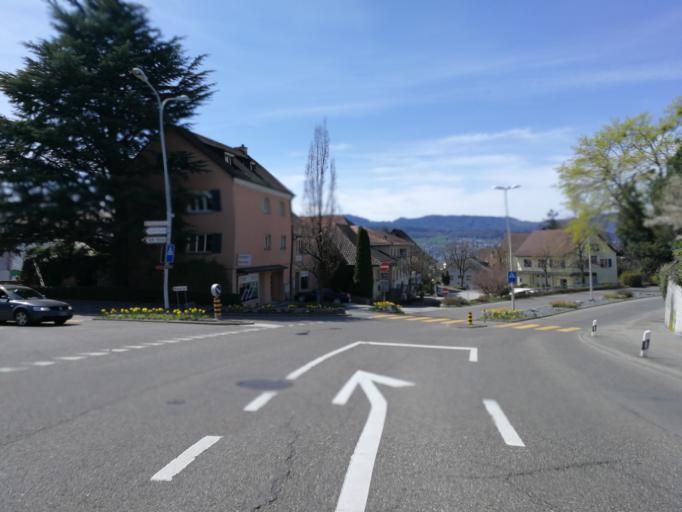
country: CH
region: Zurich
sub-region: Bezirk Meilen
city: Herrliberg
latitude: 47.2866
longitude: 8.6177
